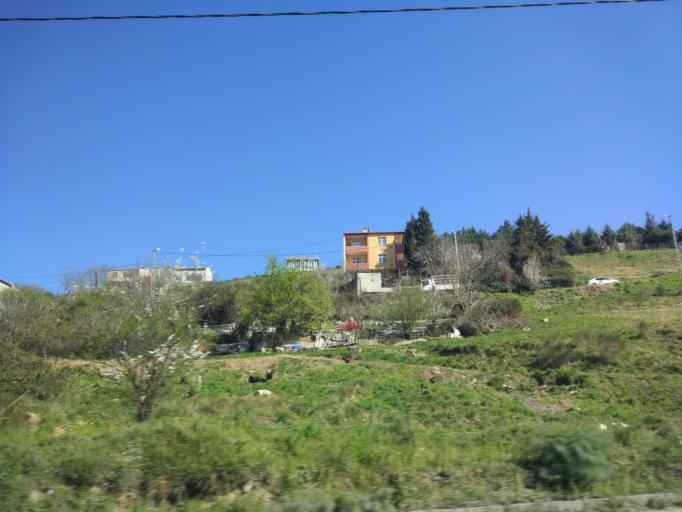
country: TR
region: Istanbul
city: Basaksehir
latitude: 41.0497
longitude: 28.7490
